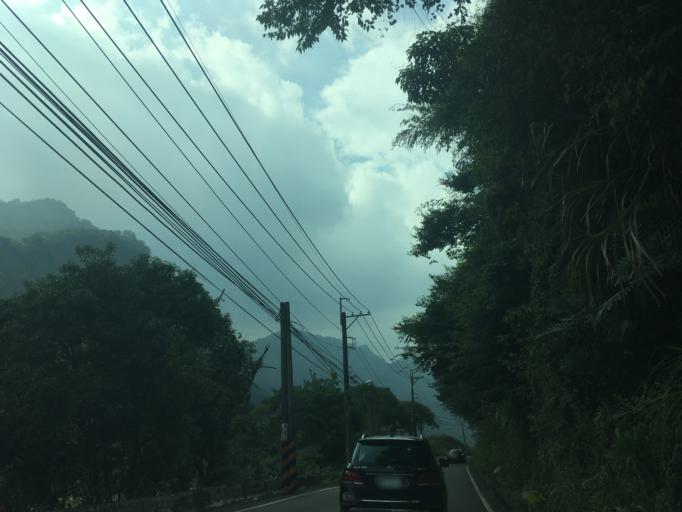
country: TW
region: Taiwan
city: Fengyuan
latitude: 24.3220
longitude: 120.9211
